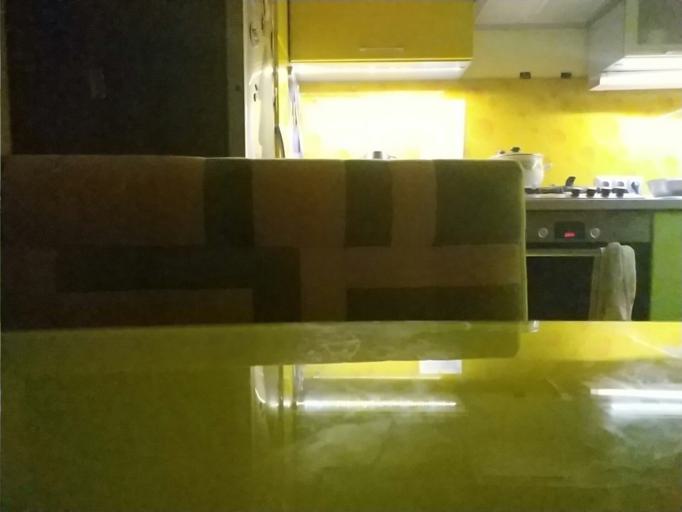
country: RU
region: Republic of Karelia
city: Pyaozerskiy
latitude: 65.7291
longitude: 30.5055
